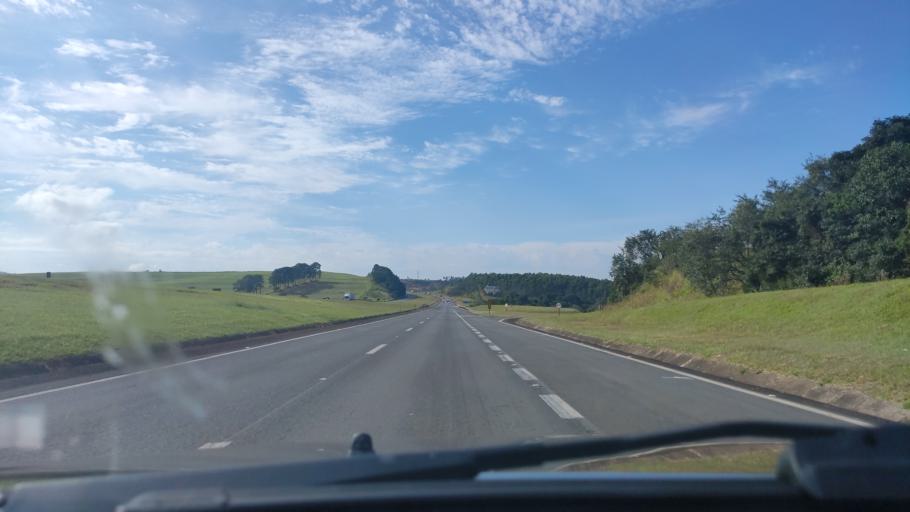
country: BR
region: Sao Paulo
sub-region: Itatinga
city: Itatinga
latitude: -23.1286
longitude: -48.4715
